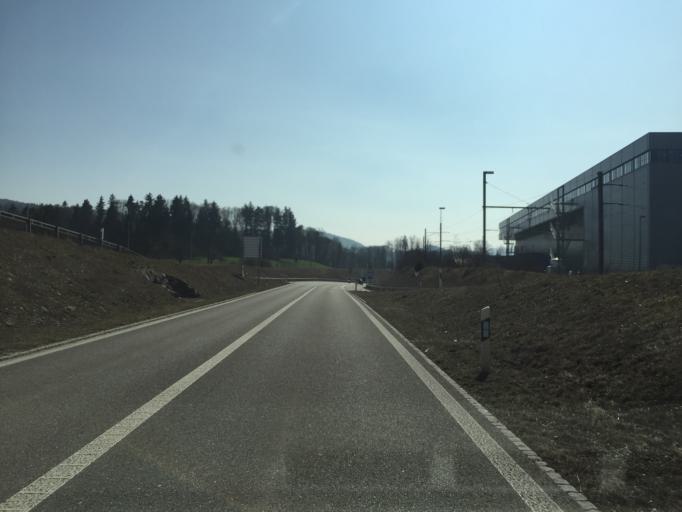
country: CH
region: Saint Gallen
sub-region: Wahlkreis Wil
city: Jonschwil
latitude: 47.4221
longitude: 9.0704
